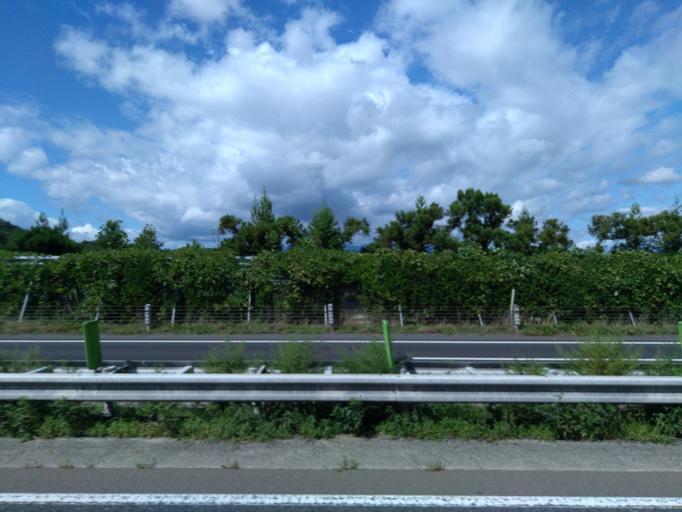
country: JP
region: Miyagi
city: Tomiya
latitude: 38.4200
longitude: 140.9172
